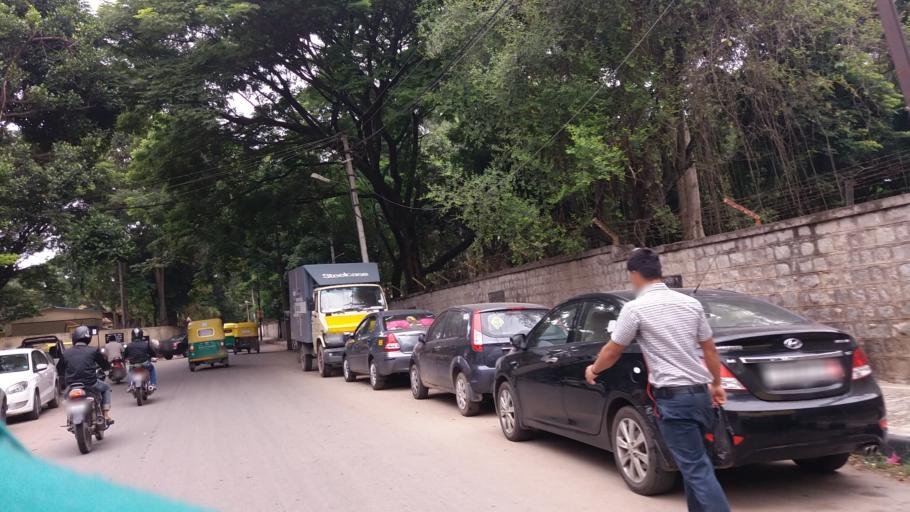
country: IN
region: Karnataka
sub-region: Bangalore Urban
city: Bangalore
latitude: 12.9723
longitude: 77.6261
